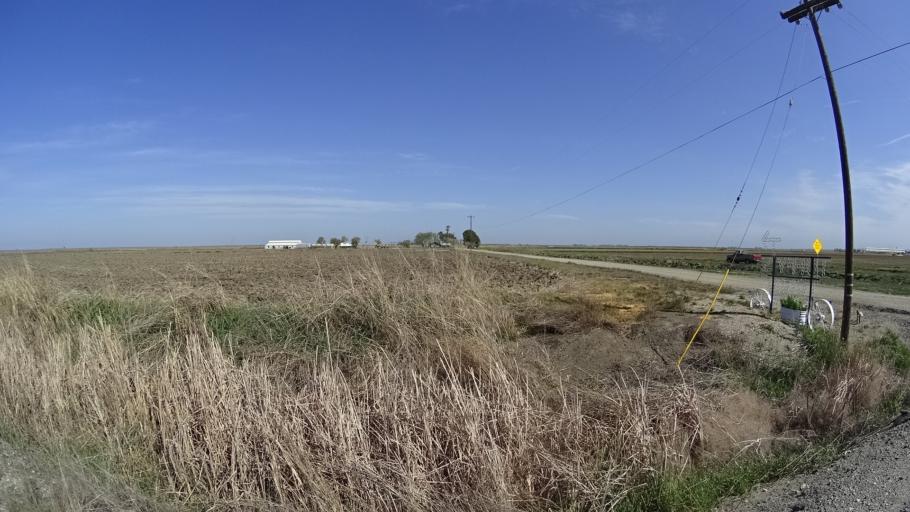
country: US
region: California
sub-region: Glenn County
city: Hamilton City
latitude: 39.6162
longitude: -122.0746
